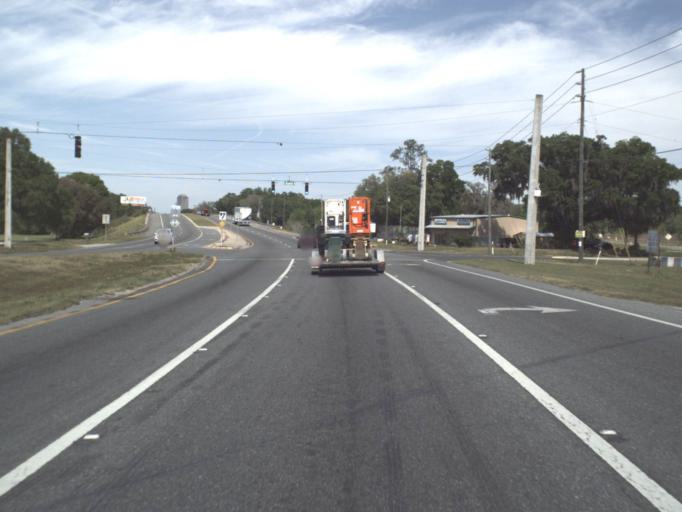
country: US
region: Florida
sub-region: Marion County
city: Belleview
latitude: 29.0536
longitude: -82.0401
